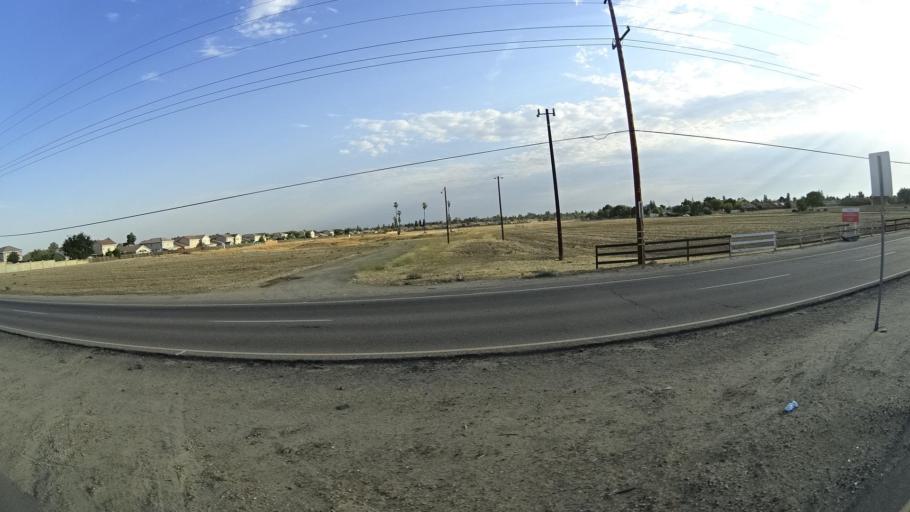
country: US
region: California
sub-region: Fresno County
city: Sunnyside
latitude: 36.7068
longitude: -119.7092
